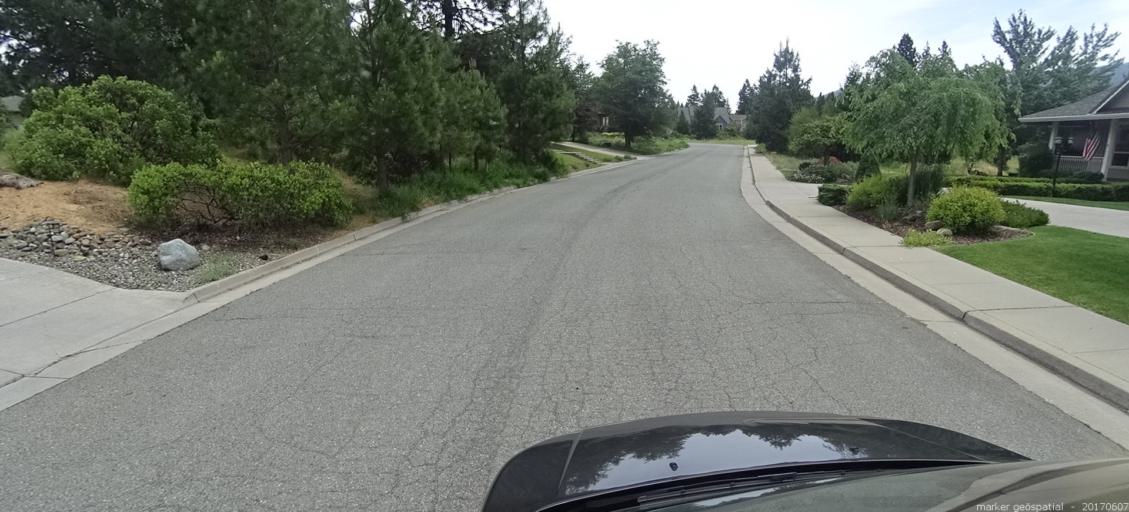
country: US
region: California
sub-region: Siskiyou County
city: Mount Shasta
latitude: 41.2933
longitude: -122.3148
